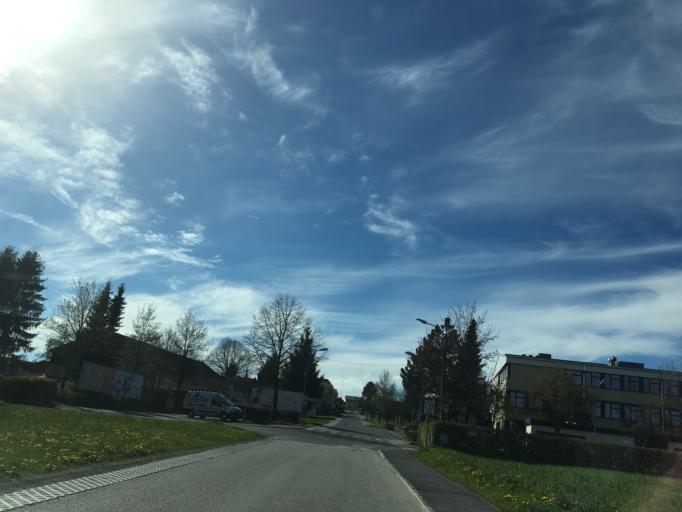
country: AT
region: Upper Austria
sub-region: Politischer Bezirk Urfahr-Umgebung
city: Bad Leonfelden
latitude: 48.5199
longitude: 14.3028
